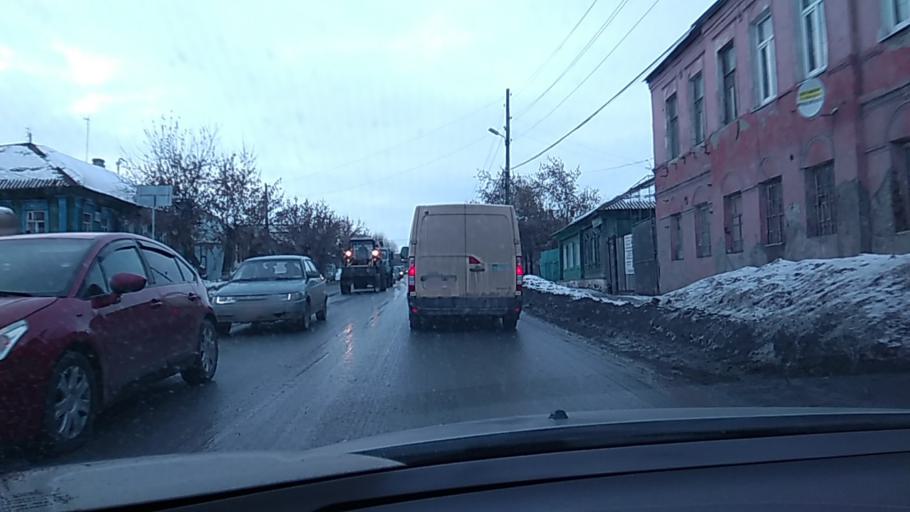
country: RU
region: Sverdlovsk
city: Martyush
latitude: 56.4178
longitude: 61.8893
